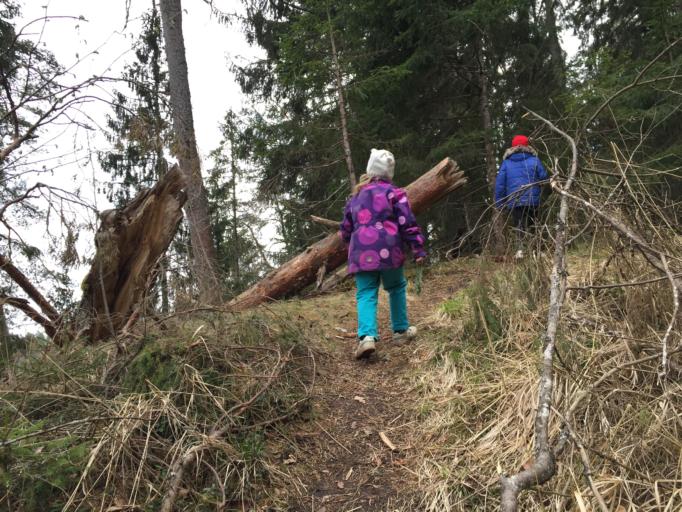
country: LV
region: Priekuli
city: Priekuli
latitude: 57.3291
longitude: 25.3931
